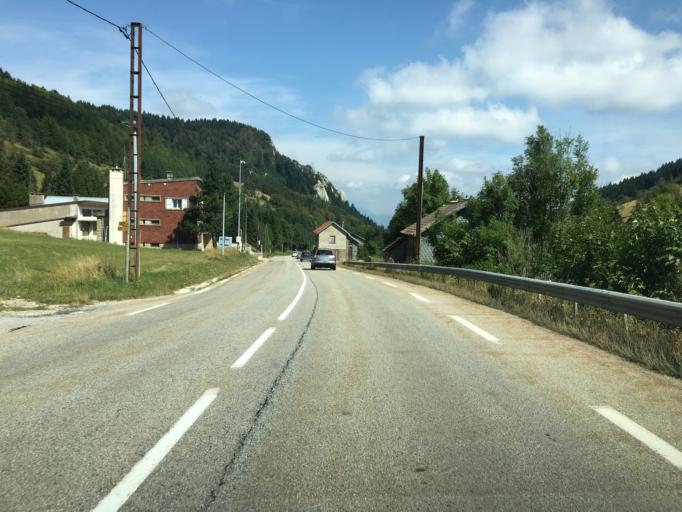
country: FR
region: Rhone-Alpes
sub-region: Departement de l'Isere
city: Mens
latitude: 44.7245
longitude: 5.6777
